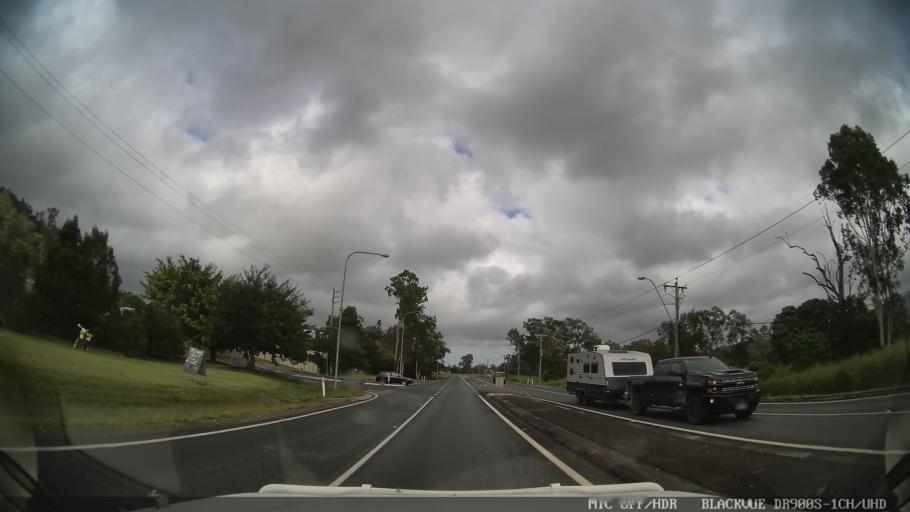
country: AU
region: Queensland
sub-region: Whitsunday
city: Proserpine
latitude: -20.3082
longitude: 148.6601
